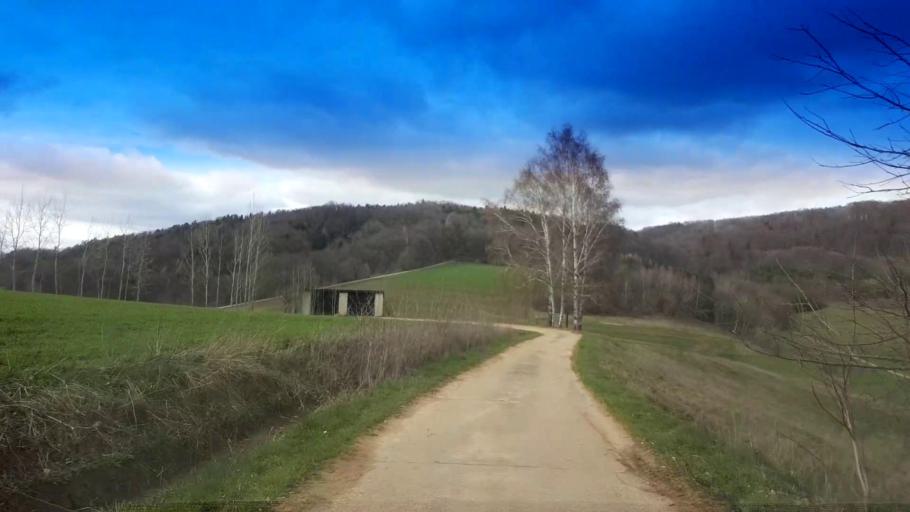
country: DE
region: Bavaria
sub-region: Upper Franconia
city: Schesslitz
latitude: 50.0084
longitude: 11.0373
